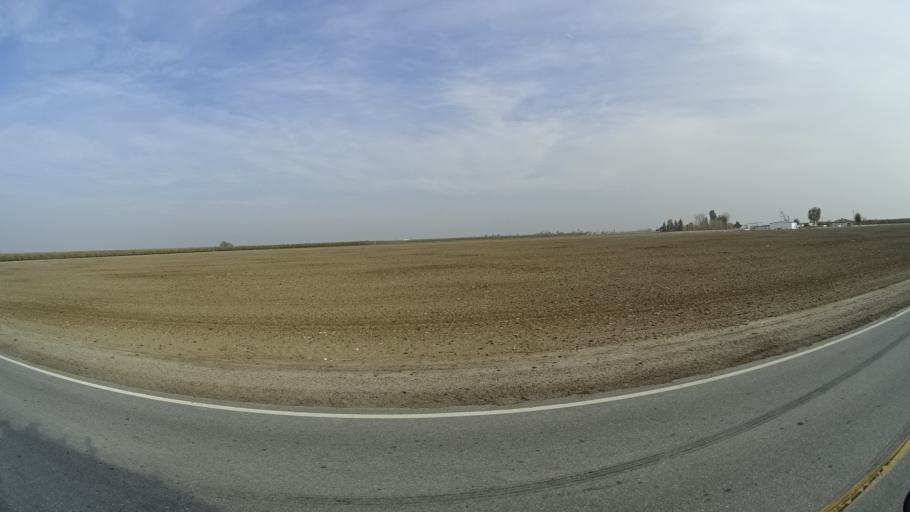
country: US
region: California
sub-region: Kern County
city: Greenacres
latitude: 35.2700
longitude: -119.1284
